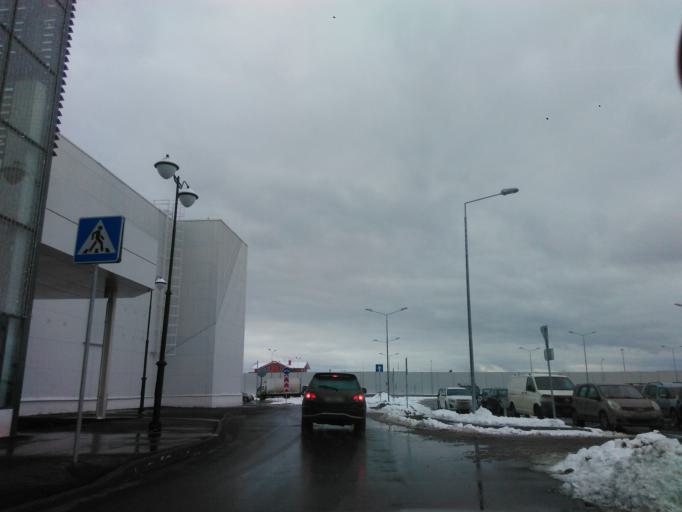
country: RU
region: Moskovskaya
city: Rzhavki
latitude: 56.0000
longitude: 37.2547
